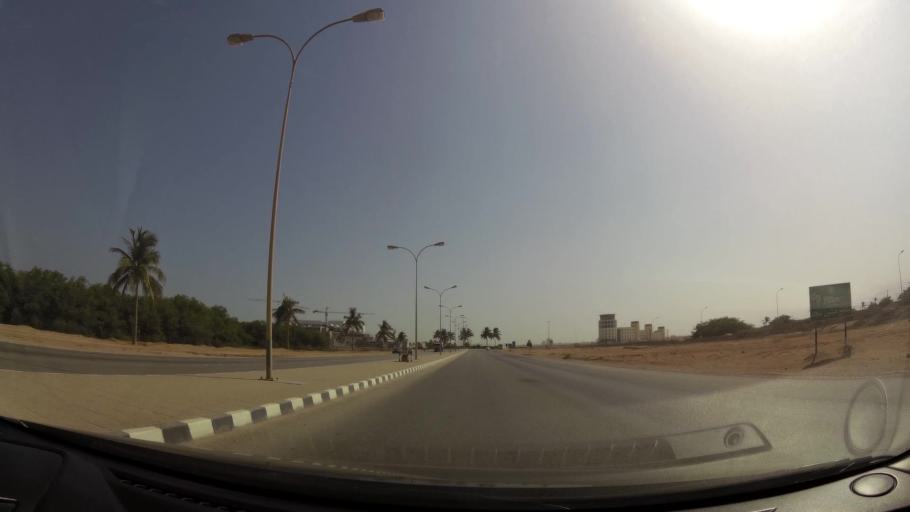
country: OM
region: Zufar
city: Salalah
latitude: 16.9864
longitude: 54.0196
